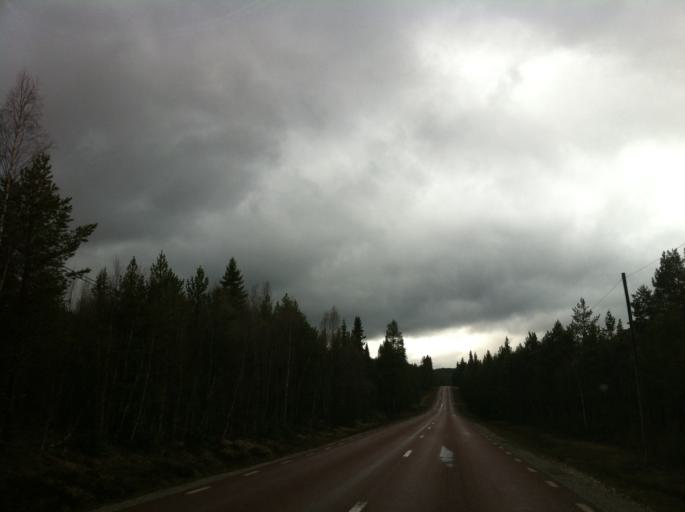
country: NO
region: Hedmark
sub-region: Engerdal
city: Engerdal
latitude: 62.4311
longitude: 12.7155
